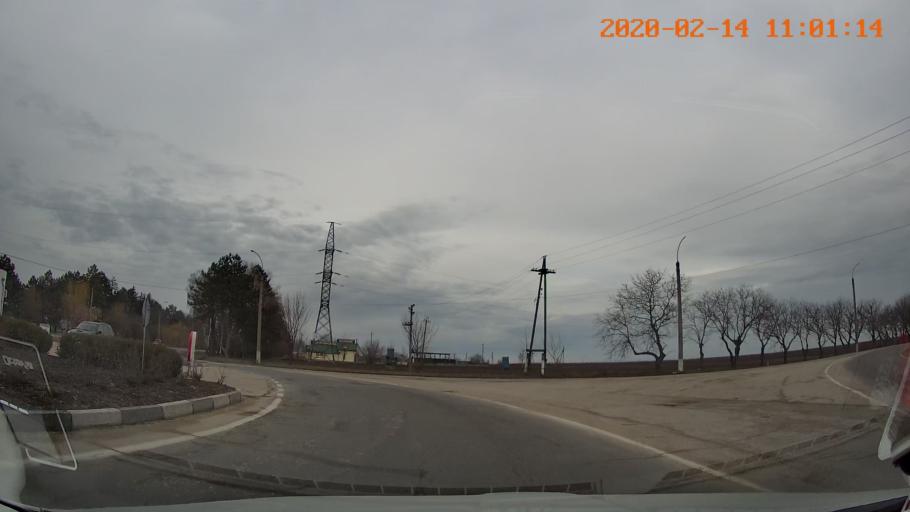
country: MD
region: Raionul Edinet
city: Edinet
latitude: 48.1590
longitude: 27.3305
